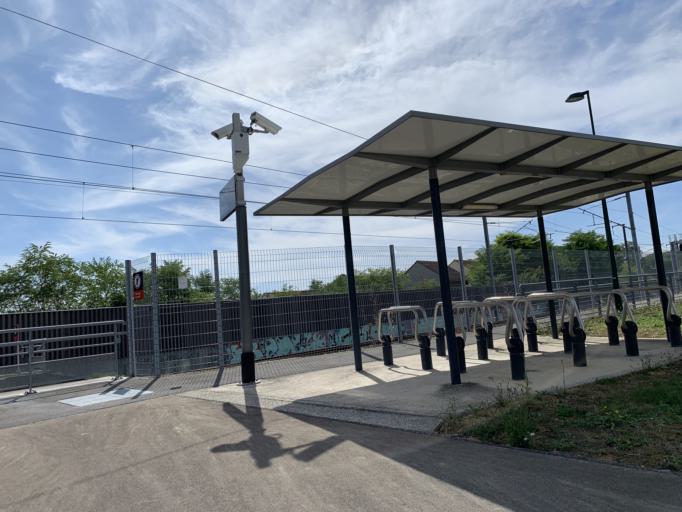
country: FR
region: Franche-Comte
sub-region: Departement du Doubs
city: Miserey-Salines
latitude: 47.2752
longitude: 5.9934
